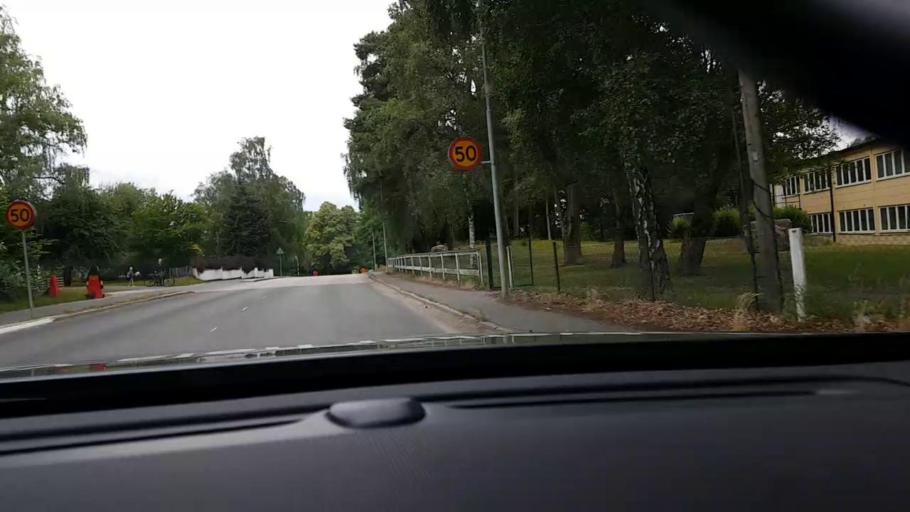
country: SE
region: Skane
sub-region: Hassleholms Kommun
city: Hassleholm
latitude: 56.1654
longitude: 13.7516
